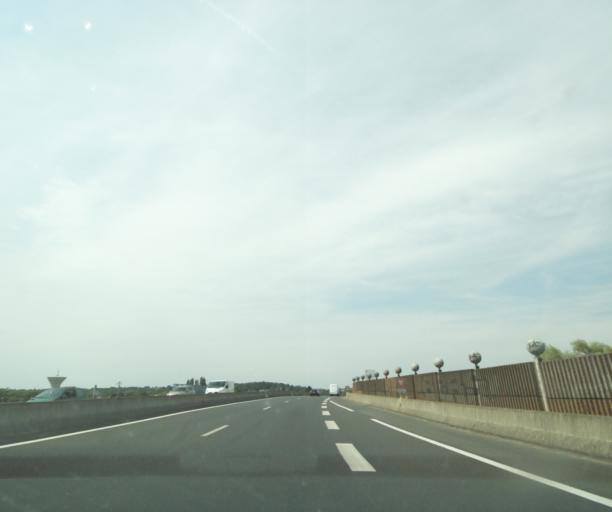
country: FR
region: Centre
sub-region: Departement d'Indre-et-Loire
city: La Riche
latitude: 47.3787
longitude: 0.6495
